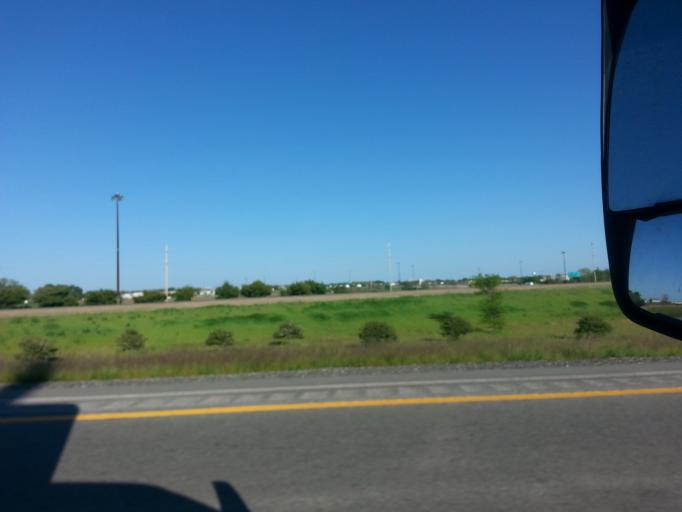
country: US
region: Illinois
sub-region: McLean County
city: Normal
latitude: 40.5423
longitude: -89.0041
